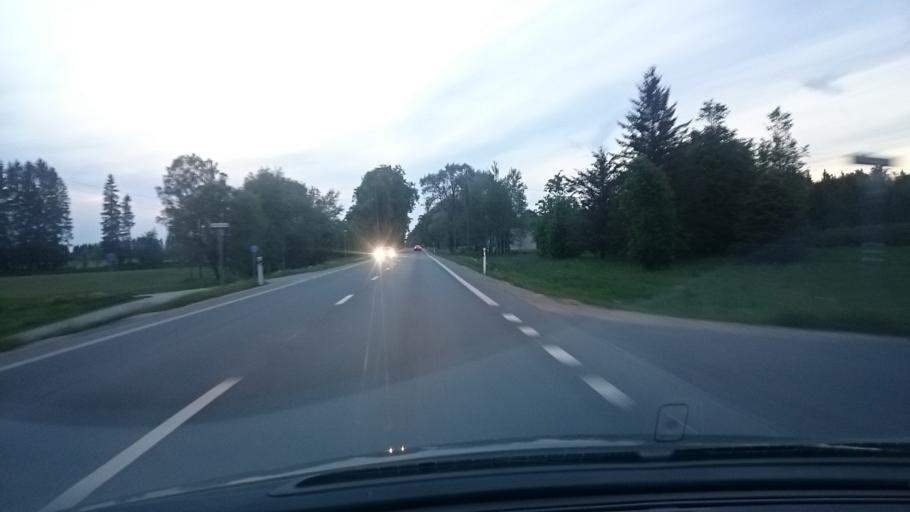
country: EE
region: Raplamaa
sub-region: Kehtna vald
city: Kehtna
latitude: 58.9751
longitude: 24.8489
